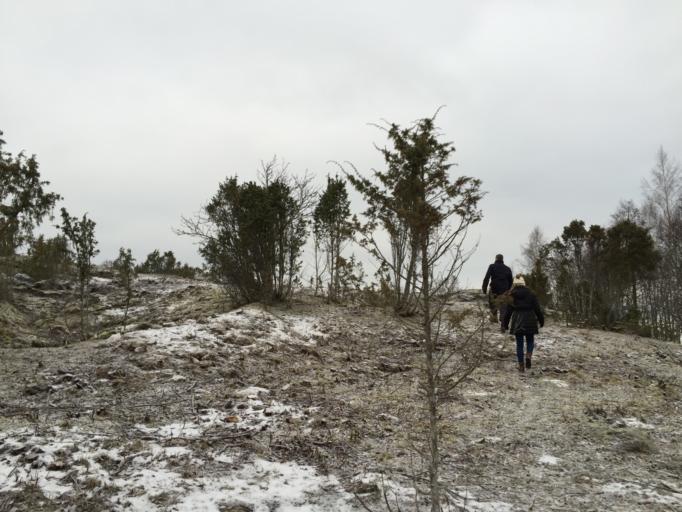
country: EE
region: Saare
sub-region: Orissaare vald
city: Orissaare
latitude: 58.6693
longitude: 23.2423
